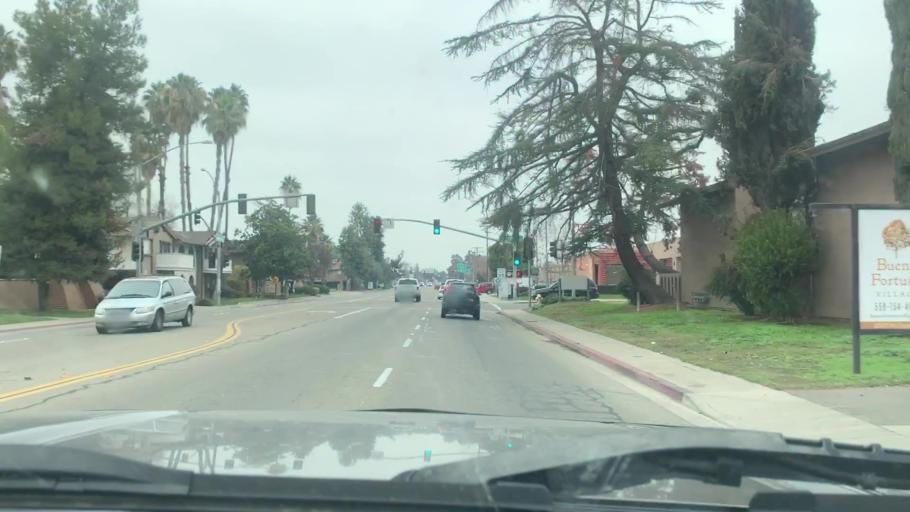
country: US
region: California
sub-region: Tulare County
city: Visalia
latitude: 36.3237
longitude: -119.3317
